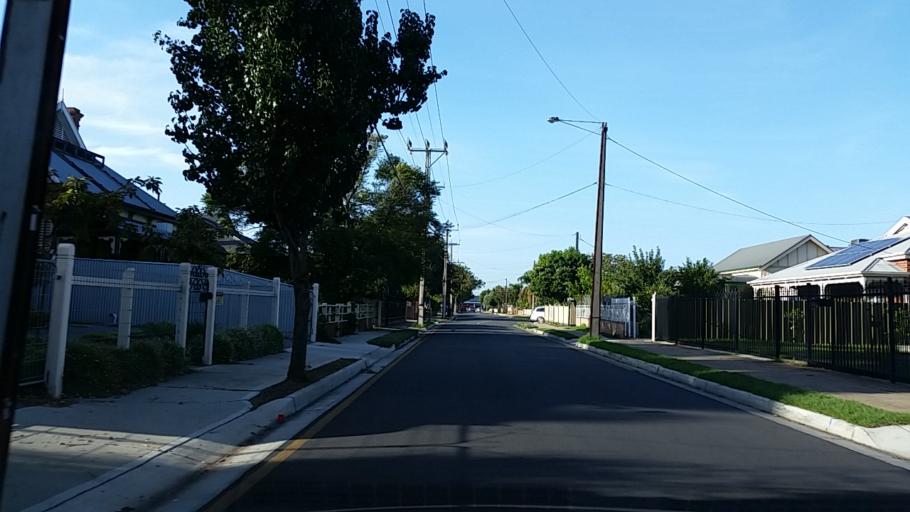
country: AU
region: South Australia
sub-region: Charles Sturt
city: Woodville
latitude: -34.8835
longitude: 138.5553
